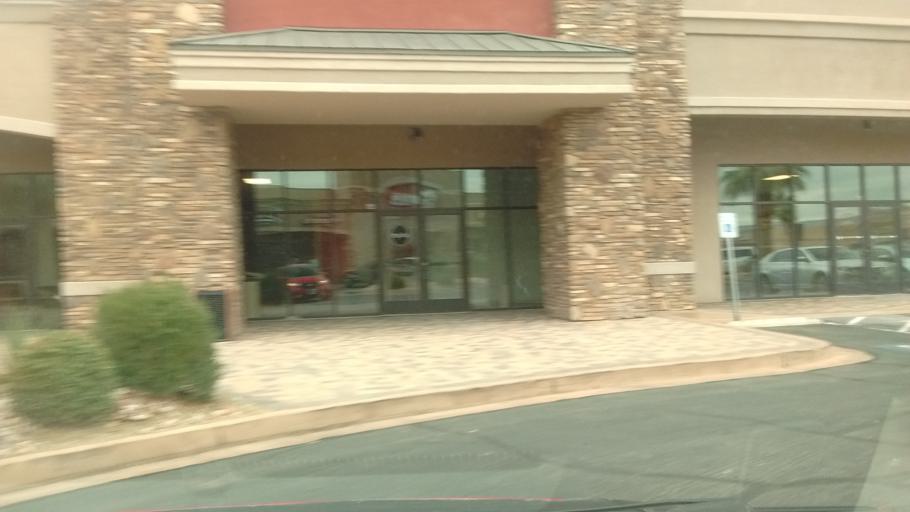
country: US
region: Utah
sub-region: Washington County
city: Washington
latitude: 37.1250
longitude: -113.5231
